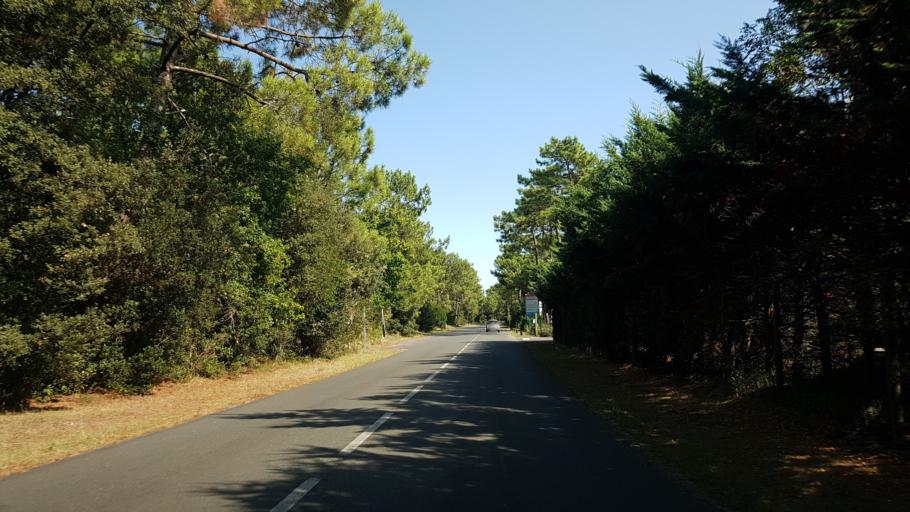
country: FR
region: Poitou-Charentes
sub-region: Departement de la Charente-Maritime
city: Les Mathes
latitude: 45.6986
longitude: -1.2012
